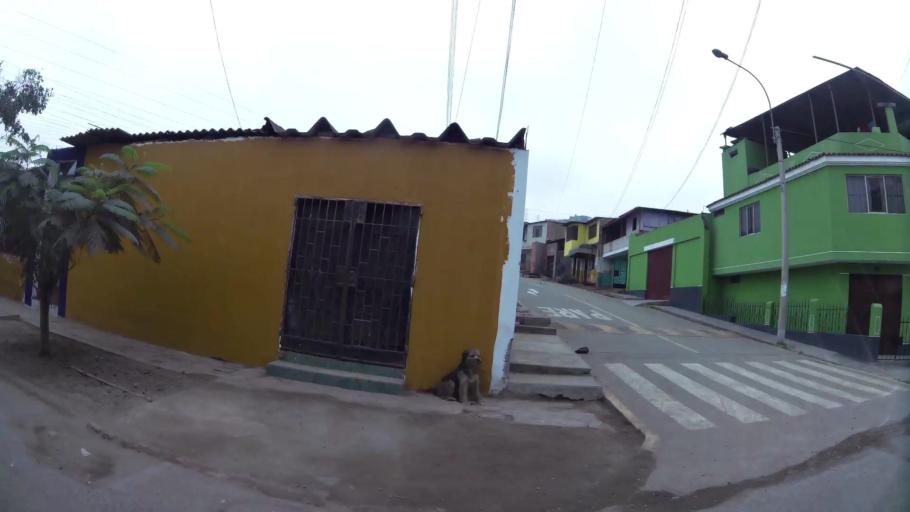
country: PE
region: Lima
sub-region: Lima
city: Surco
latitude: -12.1823
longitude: -76.9475
